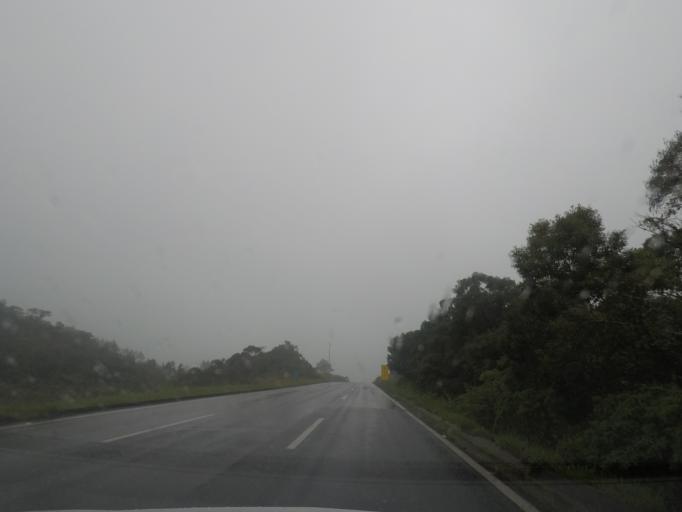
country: BR
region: Parana
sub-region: Antonina
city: Antonina
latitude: -25.1118
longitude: -48.7754
